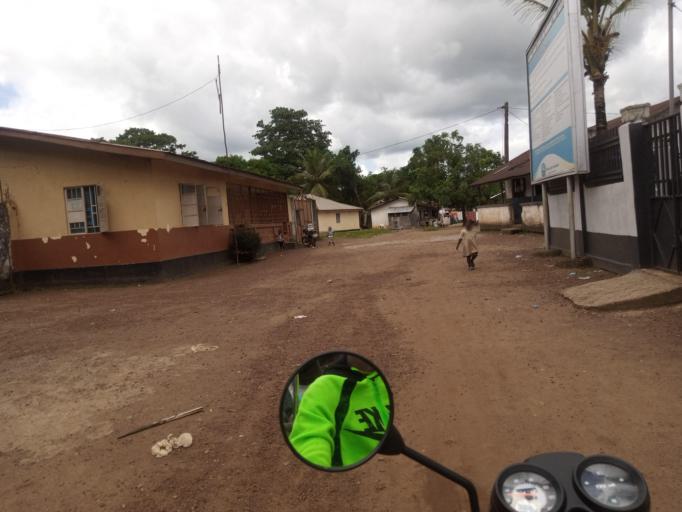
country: SL
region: Northern Province
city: Port Loko
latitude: 8.7647
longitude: -12.7841
